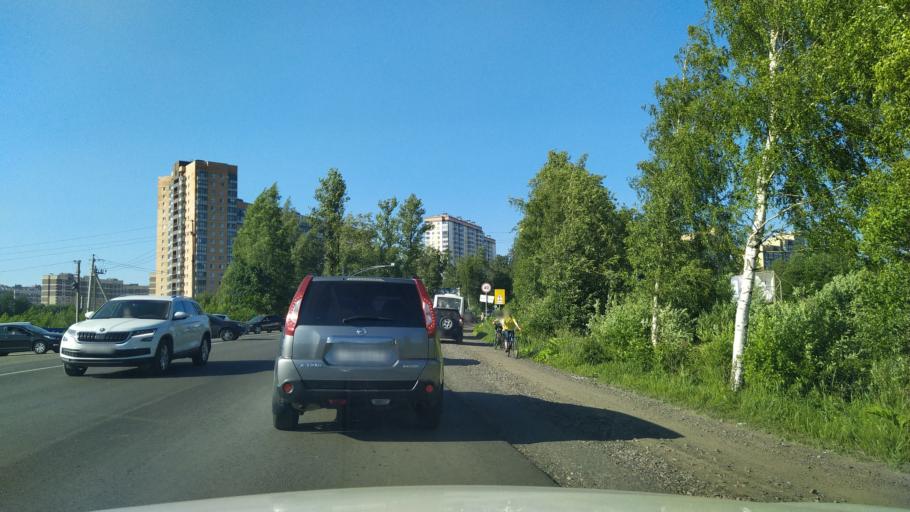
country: RU
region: Leningrad
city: Murino
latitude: 60.0533
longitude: 30.4657
